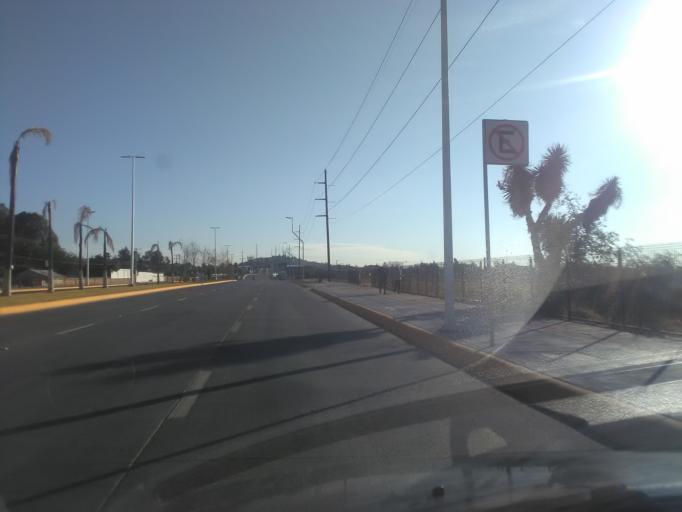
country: MX
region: Durango
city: Victoria de Durango
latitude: 24.0019
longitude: -104.6984
